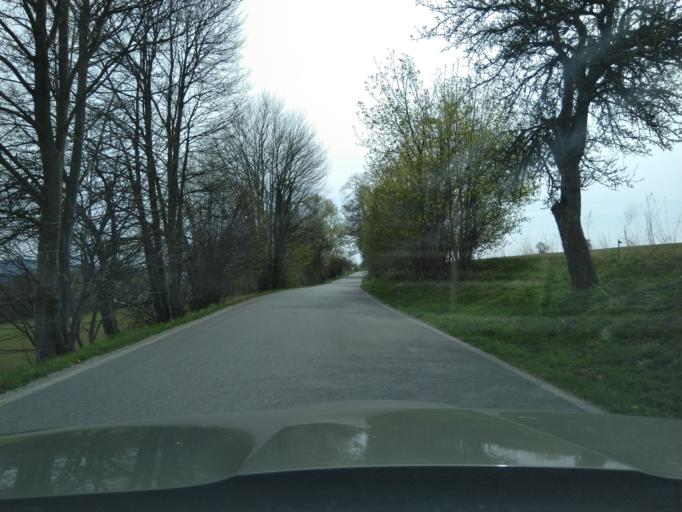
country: CZ
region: Jihocesky
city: Vacov
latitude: 49.1459
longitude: 13.7084
